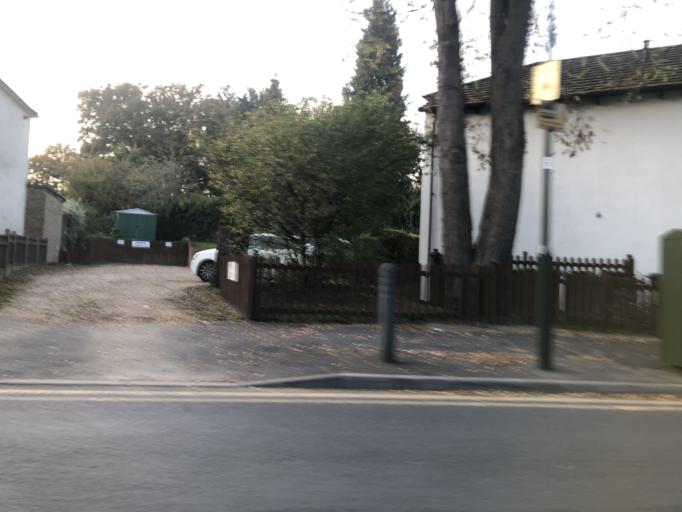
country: GB
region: England
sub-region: Greater London
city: Bexley
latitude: 51.4348
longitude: 0.1661
